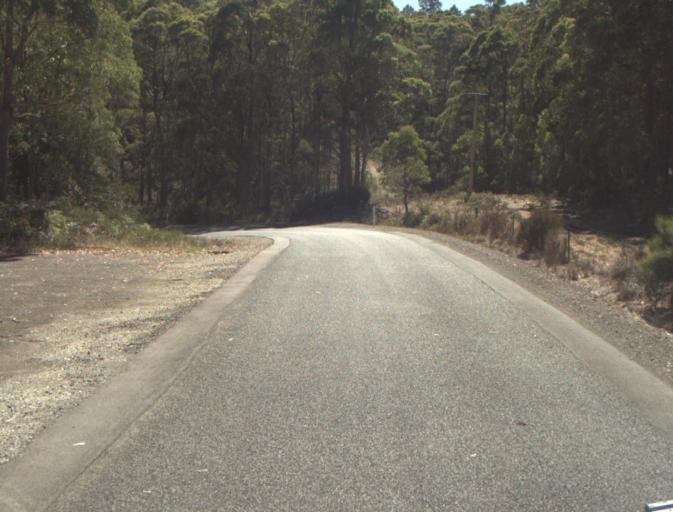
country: AU
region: Tasmania
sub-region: Launceston
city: Newstead
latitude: -41.3143
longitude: 147.3333
